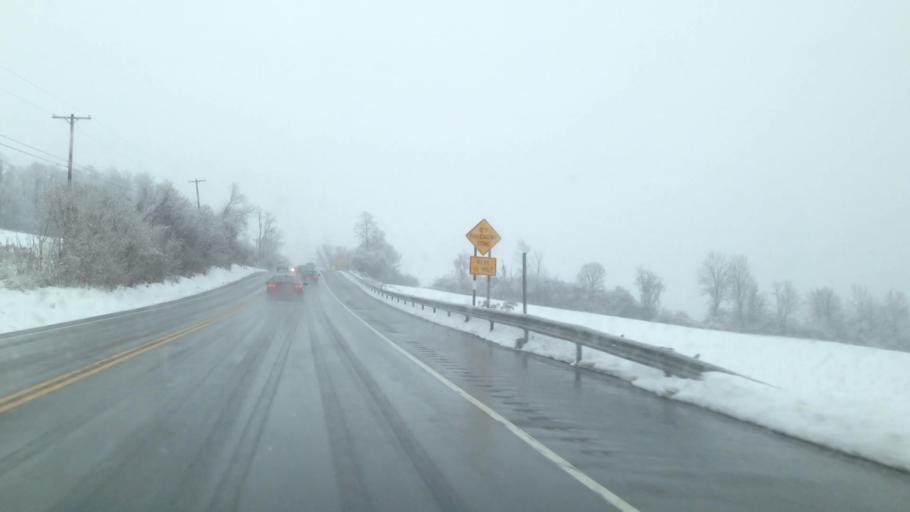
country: US
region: New York
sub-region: Onondaga County
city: Peru
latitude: 43.0348
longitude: -76.3873
